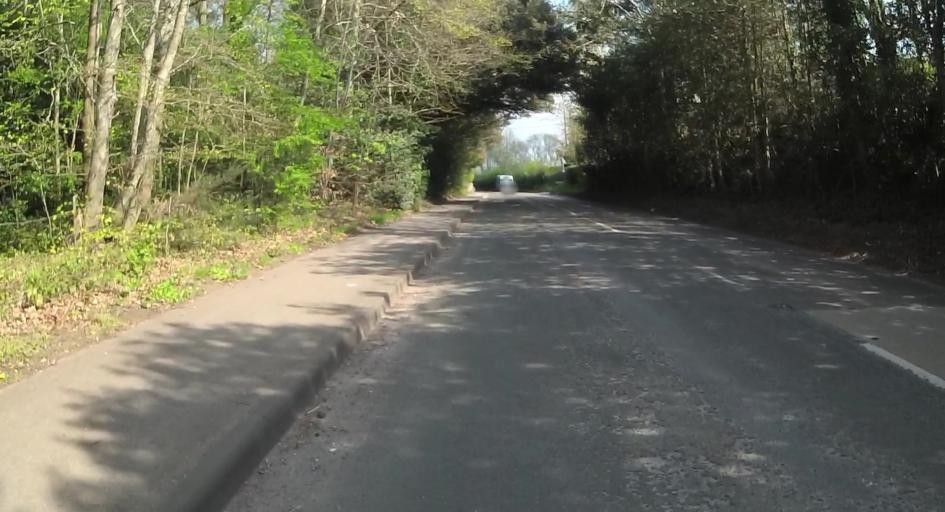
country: GB
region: England
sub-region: West Berkshire
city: Stratfield Mortimer
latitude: 51.3754
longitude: -1.0554
